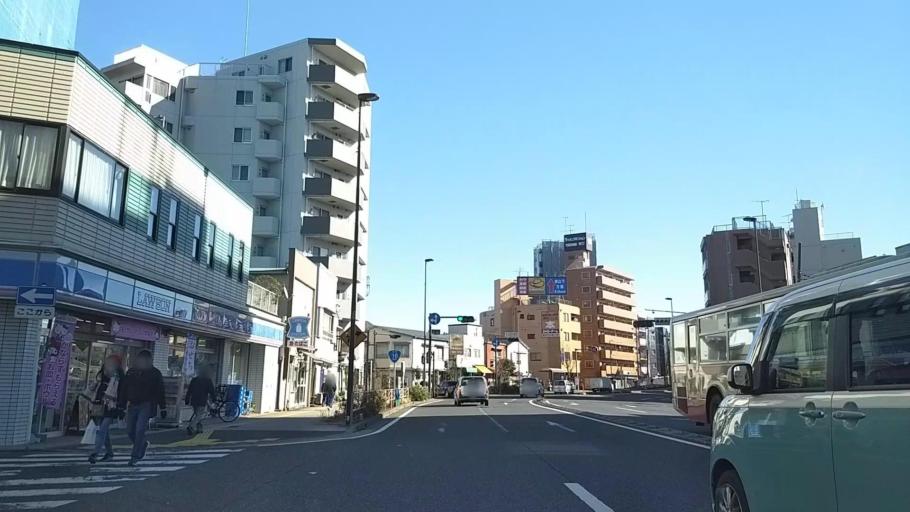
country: JP
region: Kanagawa
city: Yokohama
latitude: 35.4565
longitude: 139.6070
